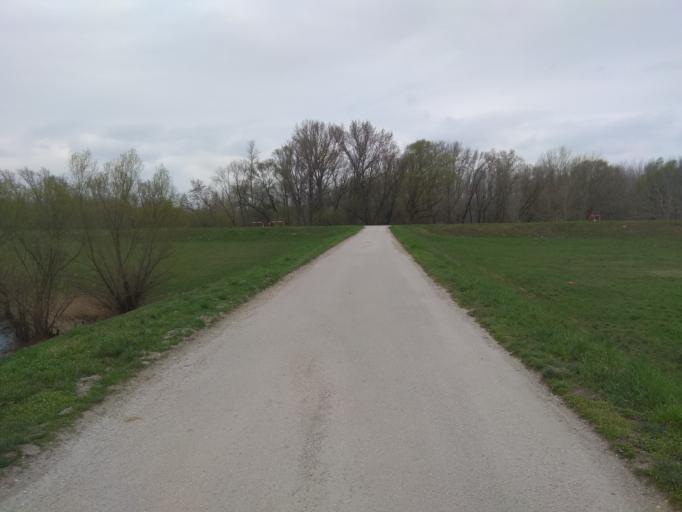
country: HU
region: Gyor-Moson-Sopron
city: Gyor
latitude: 47.7967
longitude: 17.6604
